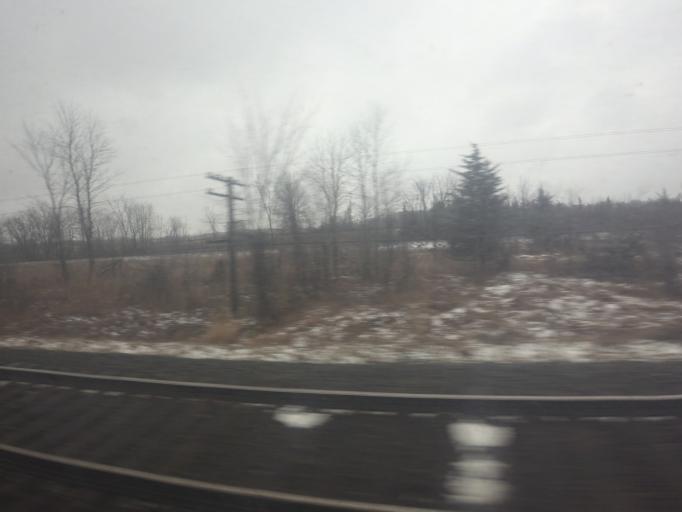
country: CA
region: Ontario
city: Quinte West
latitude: 44.0627
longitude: -77.6734
